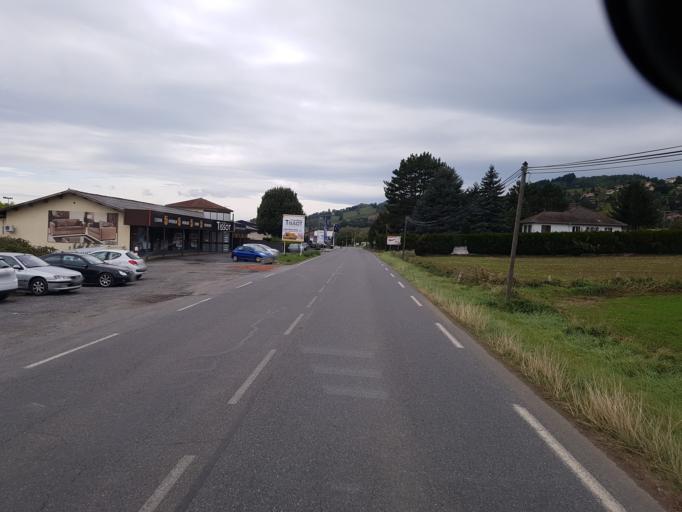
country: FR
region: Rhone-Alpes
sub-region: Departement du Rhone
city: Sainte-Foy-l'Argentiere
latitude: 45.7135
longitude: 4.4771
